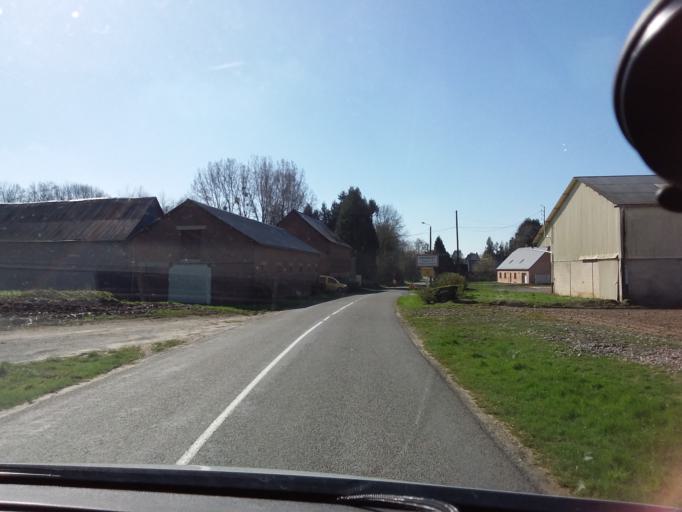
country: FR
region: Picardie
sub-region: Departement de l'Aisne
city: Montcornet
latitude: 49.7598
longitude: 4.0037
